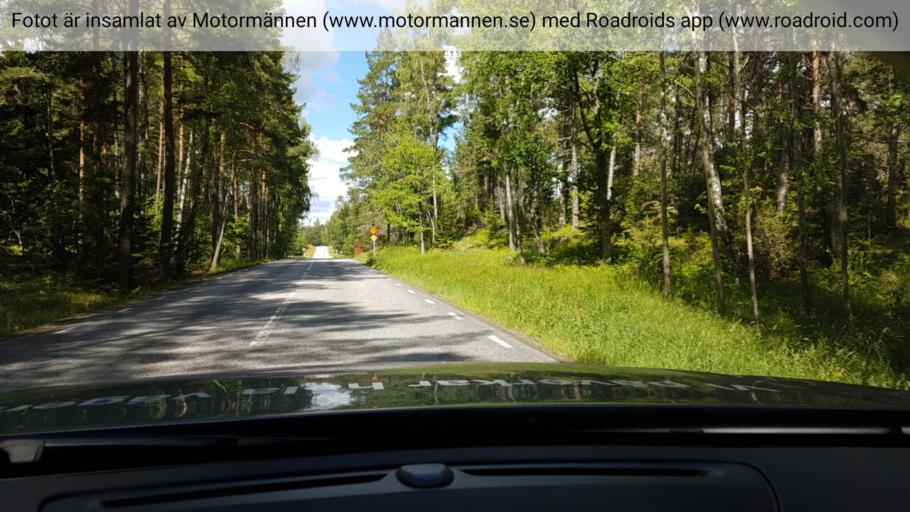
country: SE
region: Stockholm
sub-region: Varmdo Kommun
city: Hemmesta
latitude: 59.3819
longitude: 18.5222
